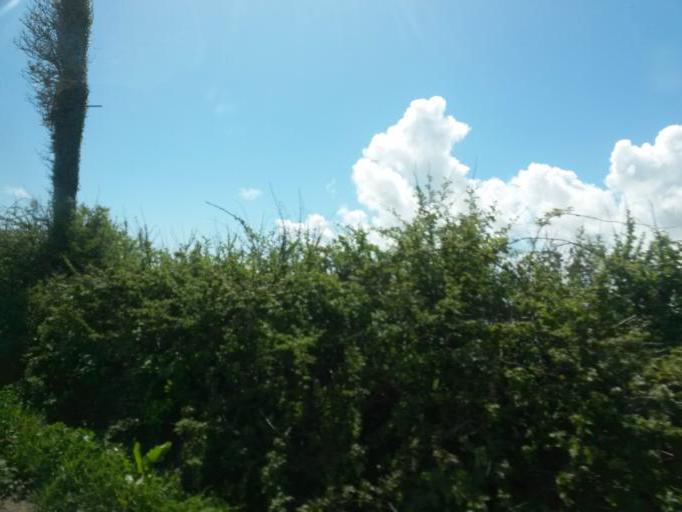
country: IE
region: Munster
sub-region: Waterford
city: Dunmore East
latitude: 52.2244
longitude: -6.9323
